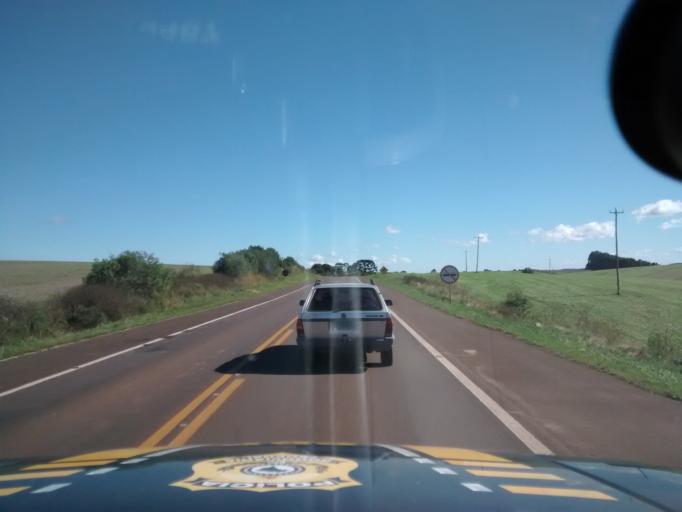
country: BR
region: Rio Grande do Sul
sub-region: Vacaria
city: Vacaria
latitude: -28.3547
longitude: -51.1295
